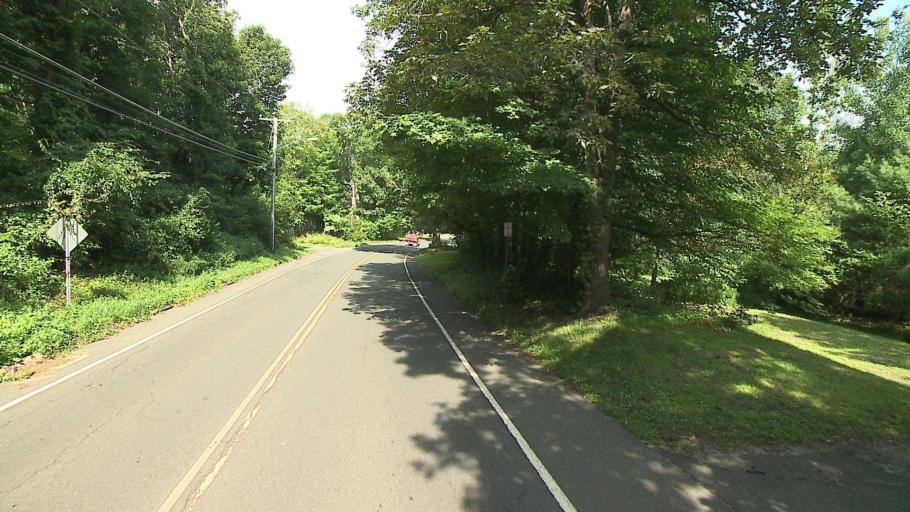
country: US
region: New York
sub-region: Putnam County
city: Putnam Lake
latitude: 41.4351
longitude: -73.4957
